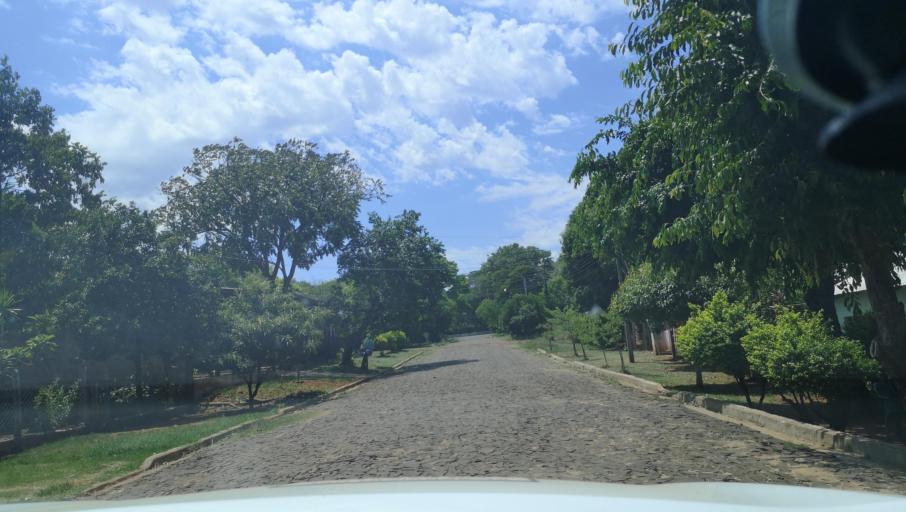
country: PY
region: Itapua
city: Carmen del Parana
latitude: -27.1640
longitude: -56.2322
